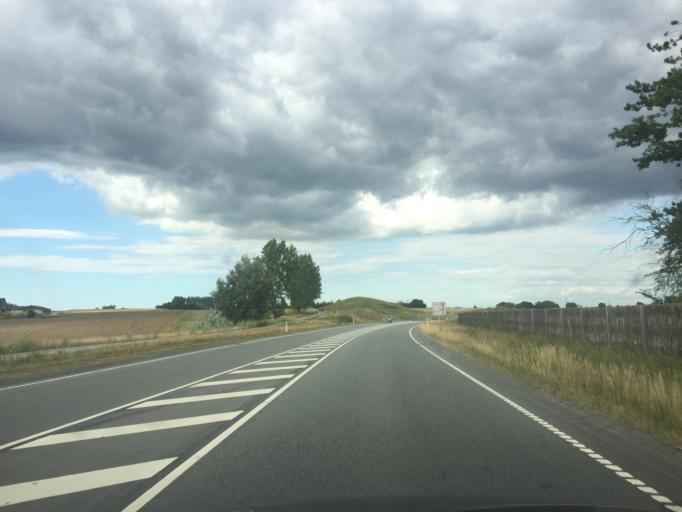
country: DK
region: Capital Region
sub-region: Frederikssund Kommune
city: Slangerup
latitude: 55.8729
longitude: 12.1915
